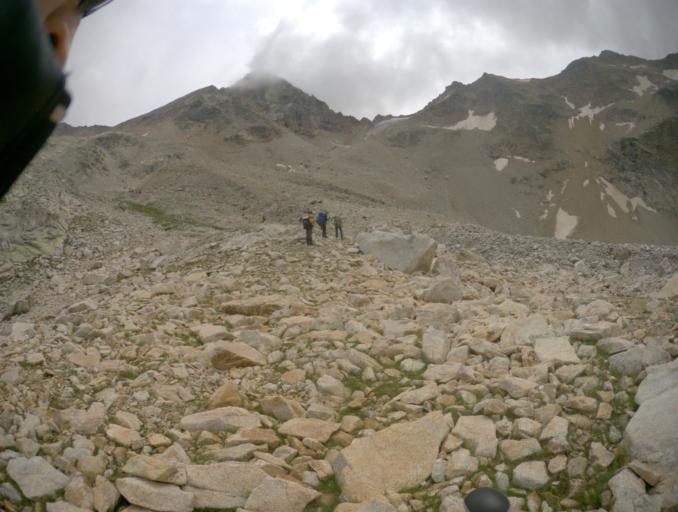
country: RU
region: Karachayevo-Cherkesiya
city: Uchkulan
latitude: 43.2821
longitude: 42.1041
